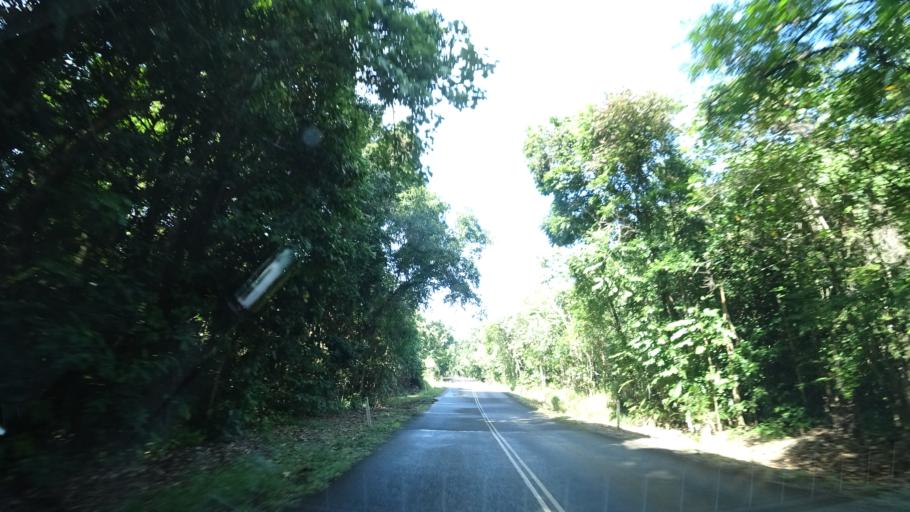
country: AU
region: Queensland
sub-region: Cairns
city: Port Douglas
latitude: -16.1495
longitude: 145.4408
